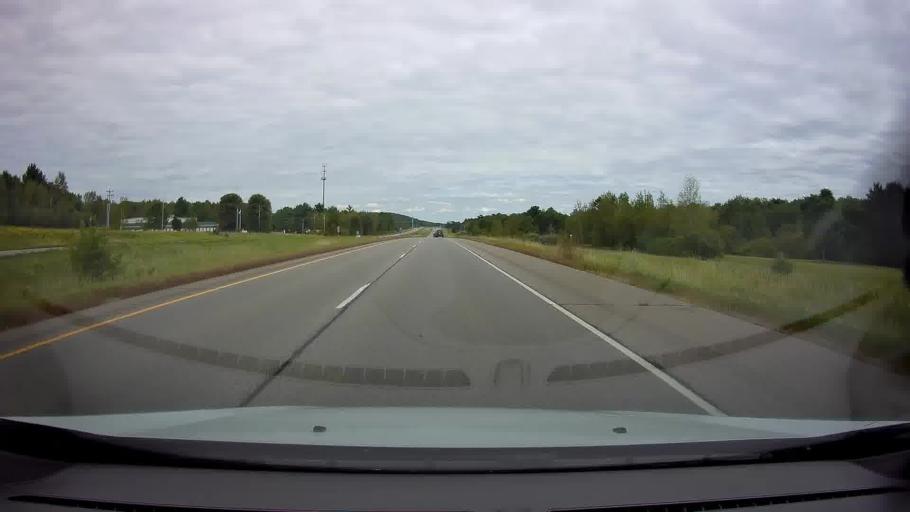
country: US
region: Wisconsin
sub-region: Marathon County
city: Rib Mountain
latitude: 44.9495
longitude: -89.7462
